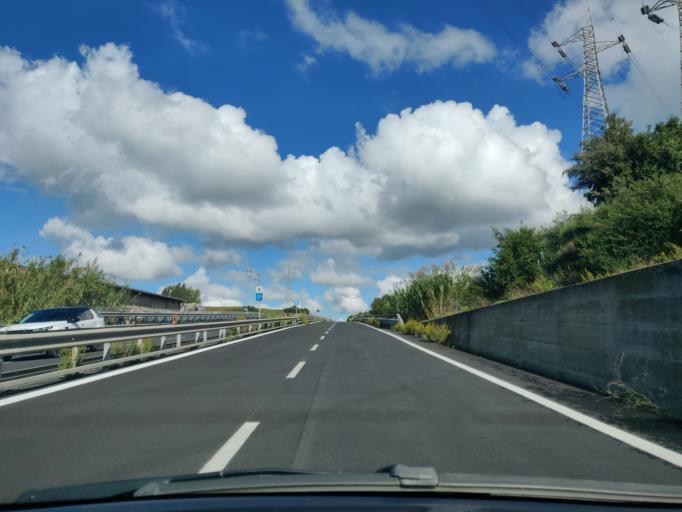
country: IT
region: Latium
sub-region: Citta metropolitana di Roma Capitale
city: Civitavecchia
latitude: 42.1097
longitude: 11.7927
